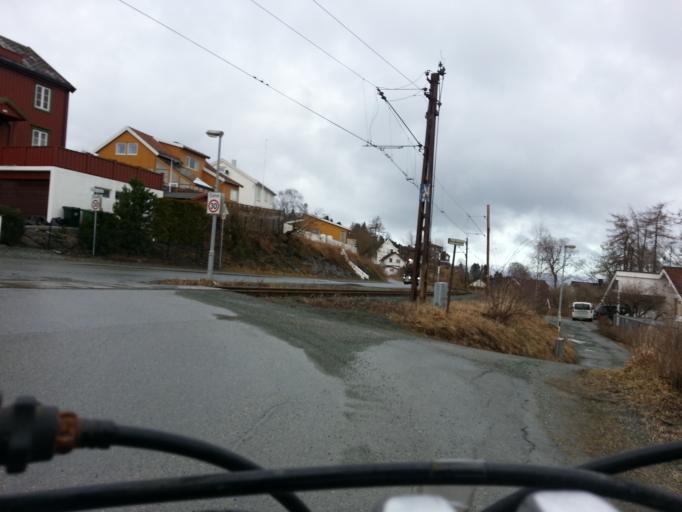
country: NO
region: Sor-Trondelag
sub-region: Trondheim
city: Trondheim
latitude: 63.4131
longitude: 10.3774
